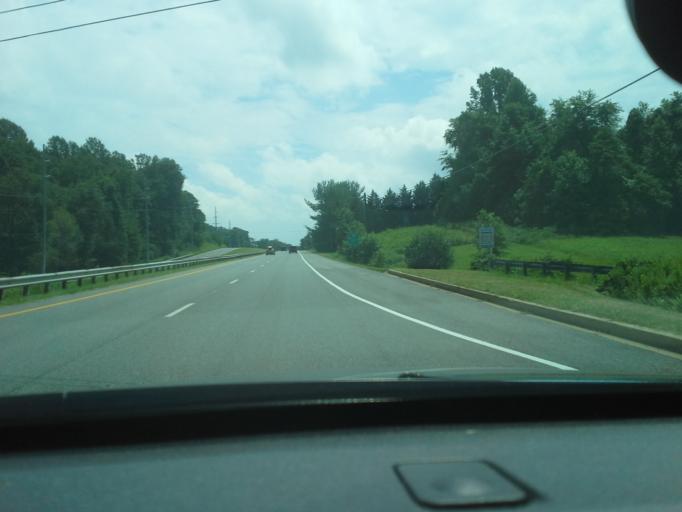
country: US
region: Maryland
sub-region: Calvert County
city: Huntingtown Town Center
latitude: 38.6671
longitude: -76.6144
